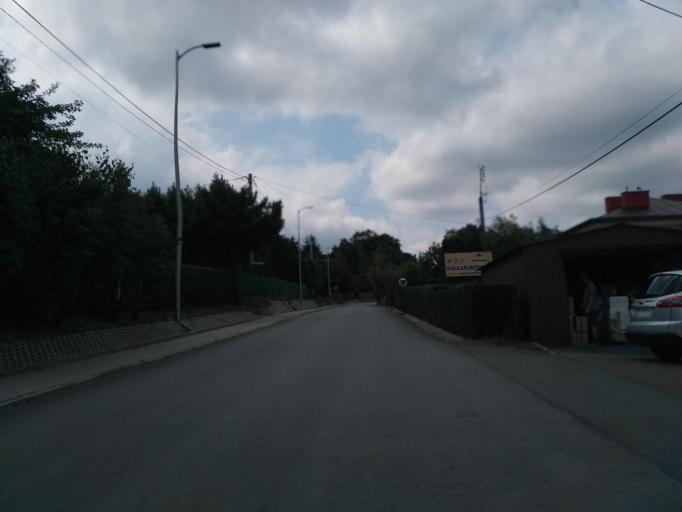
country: PL
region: Subcarpathian Voivodeship
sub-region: Powiat krosnienski
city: Iwonicz-Zdroj
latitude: 49.5714
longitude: 21.8181
